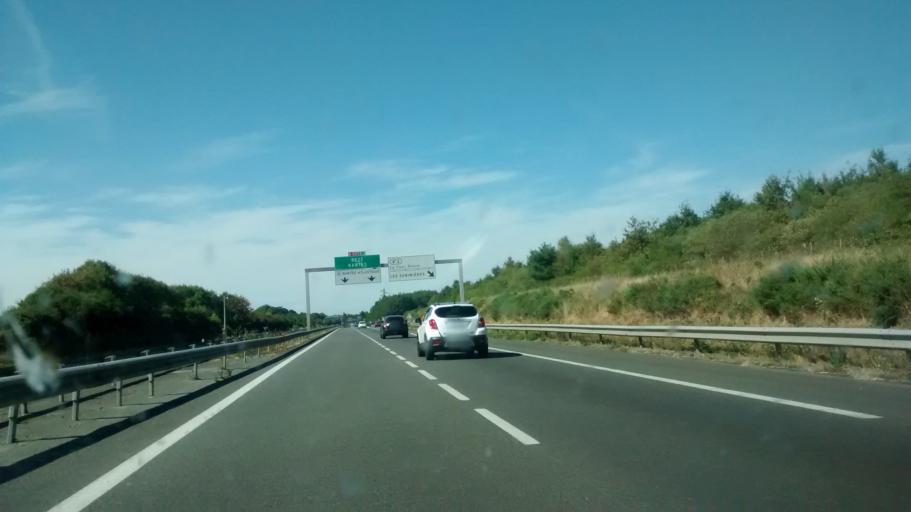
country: FR
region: Pays de la Loire
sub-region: Departement de la Loire-Atlantique
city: Le Bignon
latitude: 47.1262
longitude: -1.5021
